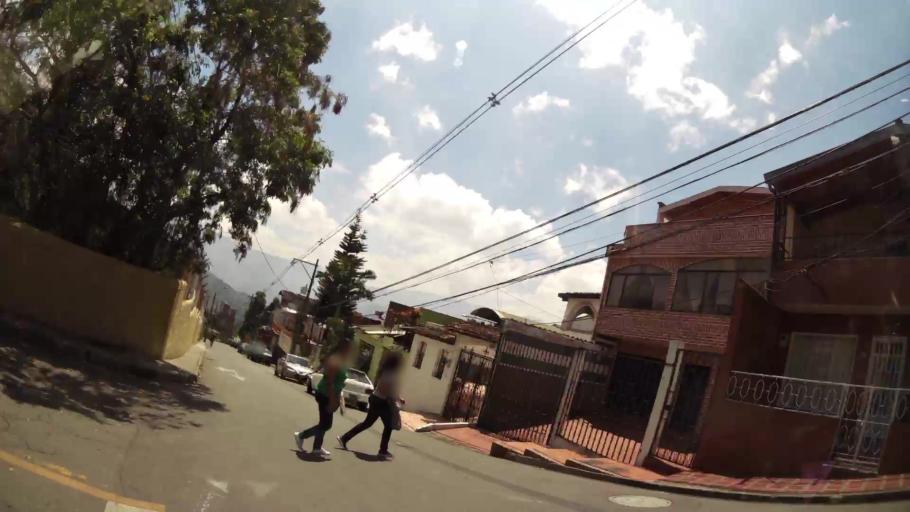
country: CO
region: Antioquia
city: La Estrella
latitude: 6.1830
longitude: -75.6578
